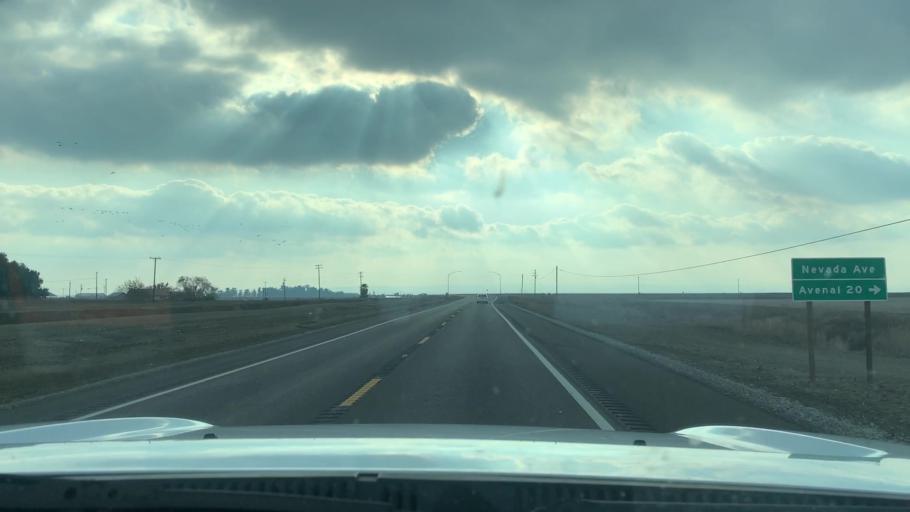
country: US
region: California
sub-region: Kings County
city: Stratford
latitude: 36.1399
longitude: -119.8764
